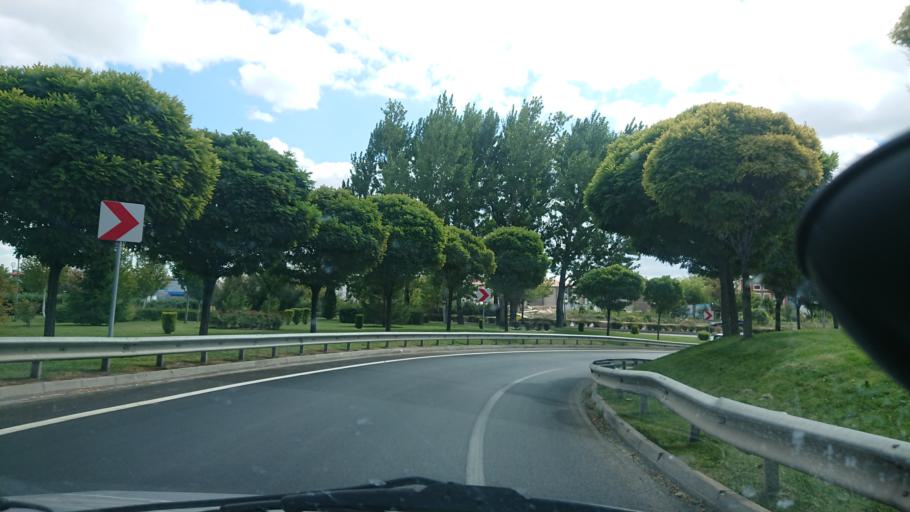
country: TR
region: Eskisehir
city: Eskisehir
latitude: 39.7821
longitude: 30.4854
